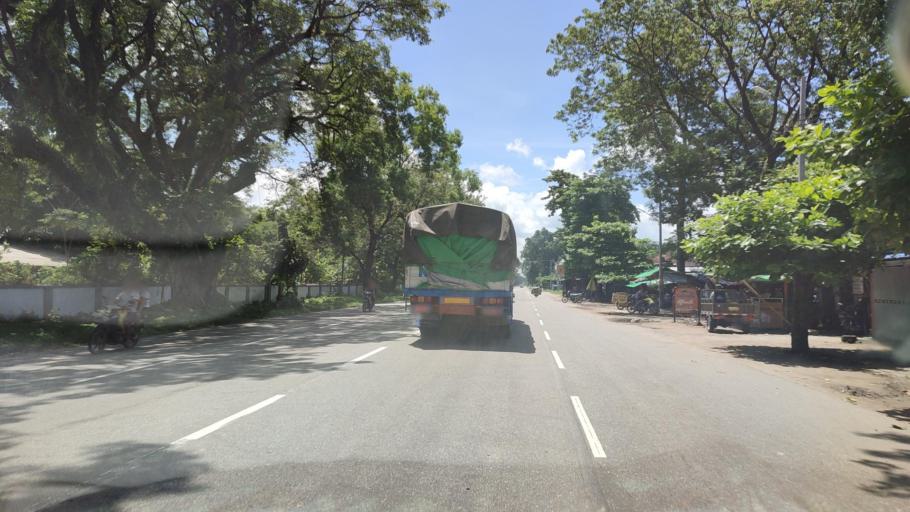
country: MM
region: Bago
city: Taungoo
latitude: 19.0217
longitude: 96.3789
